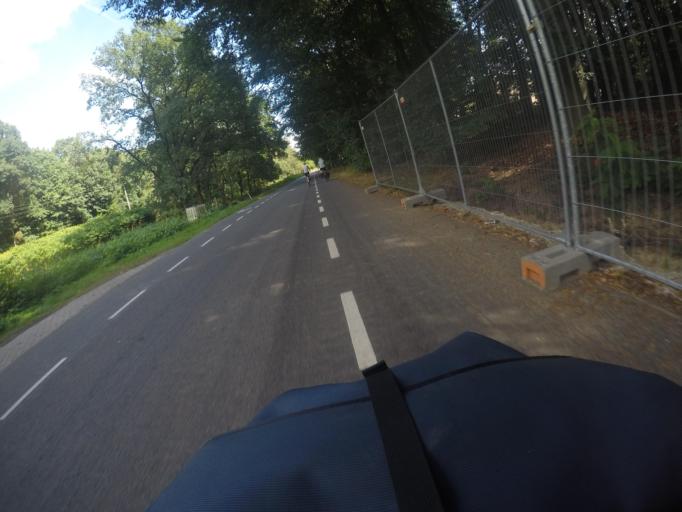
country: NL
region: Gelderland
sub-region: Gemeente Renkum
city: Oosterbeek
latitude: 51.9975
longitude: 5.8322
